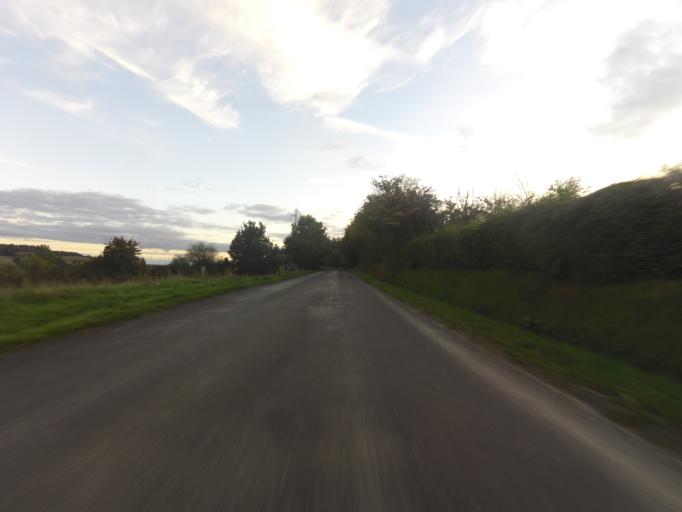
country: FR
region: Lower Normandy
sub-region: Departement de l'Orne
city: Vimoutiers
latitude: 48.9227
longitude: 0.2644
